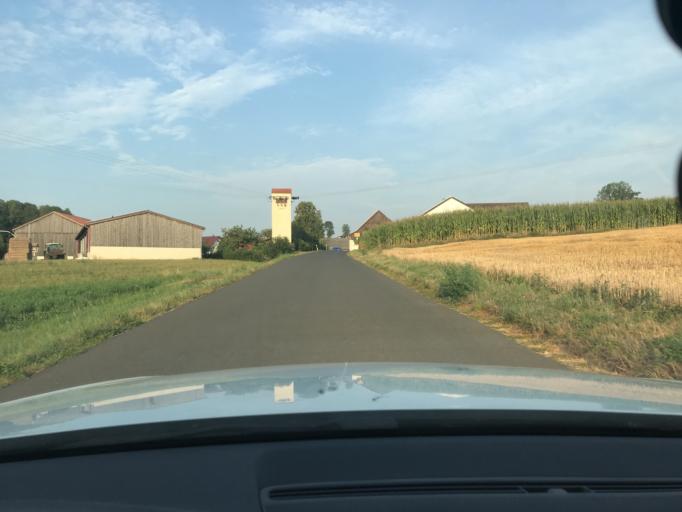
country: DE
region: Bavaria
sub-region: Upper Franconia
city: Pegnitz
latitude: 49.7371
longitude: 11.5846
